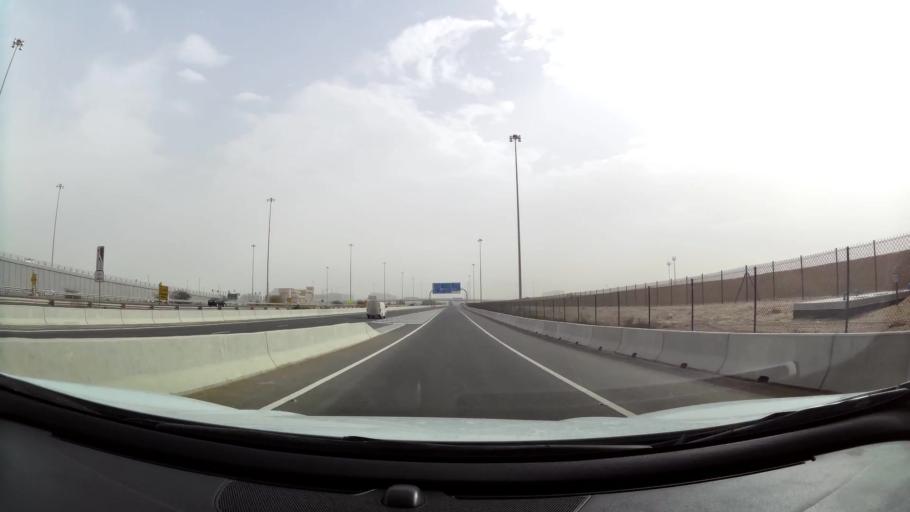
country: AE
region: Abu Dhabi
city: Abu Dhabi
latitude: 24.4408
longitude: 54.5866
